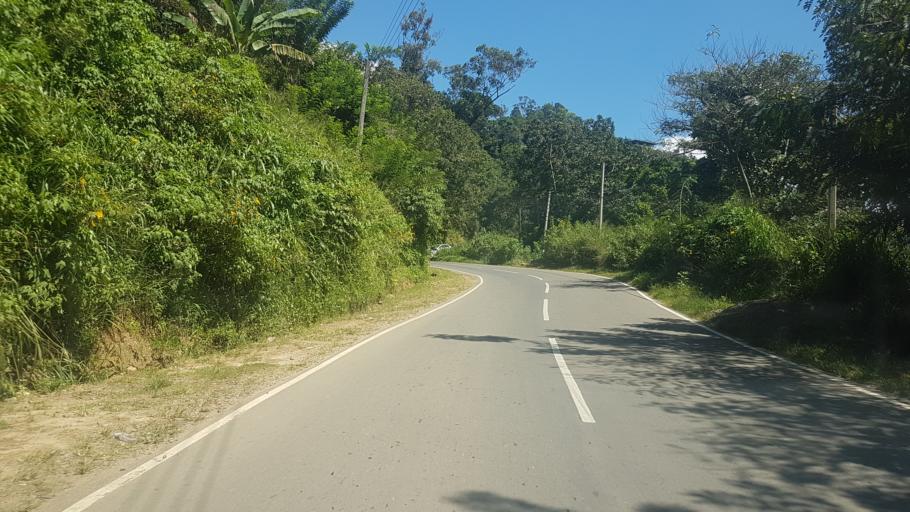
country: LK
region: Uva
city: Badulla
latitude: 6.8686
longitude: 81.0473
